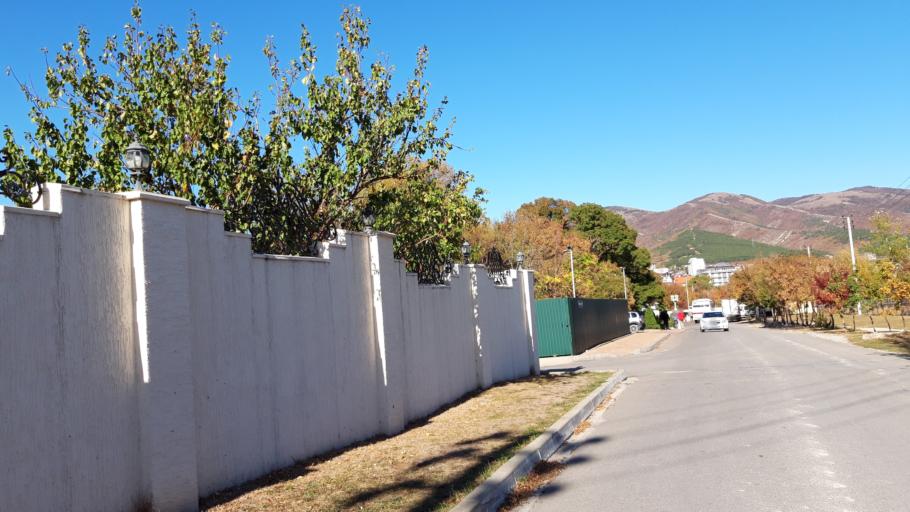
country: RU
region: Krasnodarskiy
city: Kabardinka
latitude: 44.6433
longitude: 37.9354
